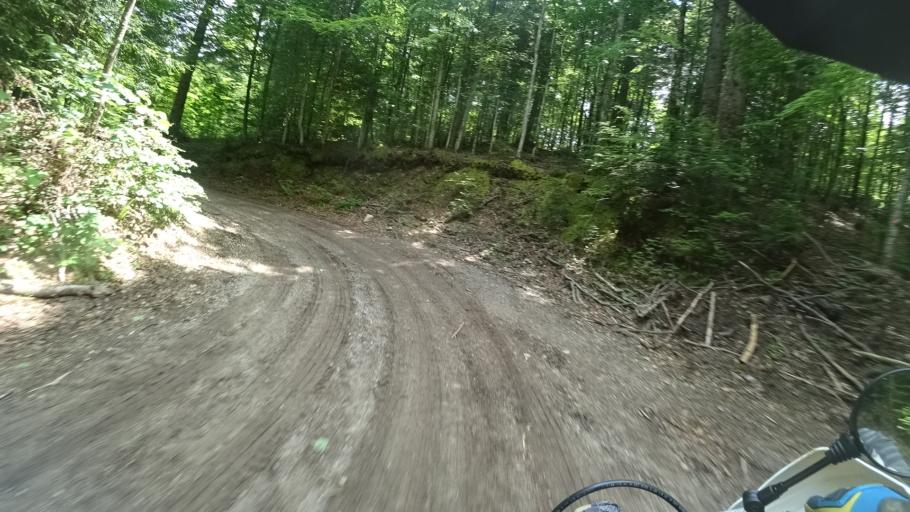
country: HR
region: Zadarska
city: Gracac
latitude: 44.4882
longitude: 15.8718
